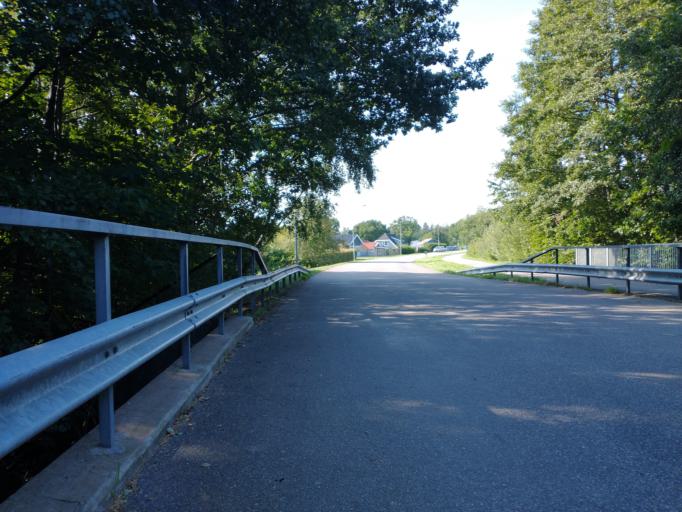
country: SE
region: Kalmar
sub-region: Kalmar Kommun
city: Lindsdal
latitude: 56.7820
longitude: 16.3023
